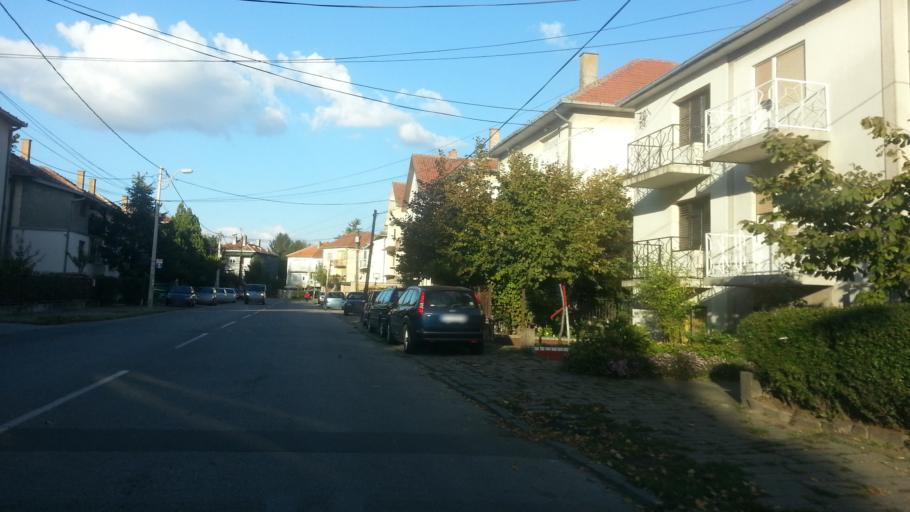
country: RS
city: Novi Banovci
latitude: 44.8999
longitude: 20.2940
